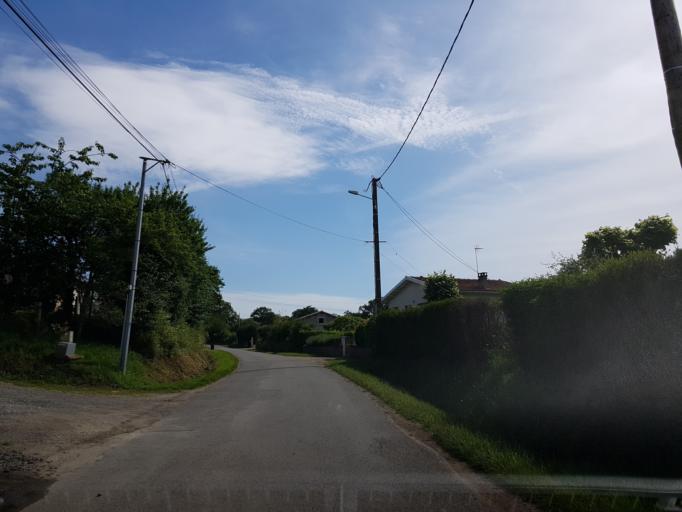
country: FR
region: Poitou-Charentes
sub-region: Departement de la Charente
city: Etagnac
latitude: 45.9352
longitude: 0.7413
